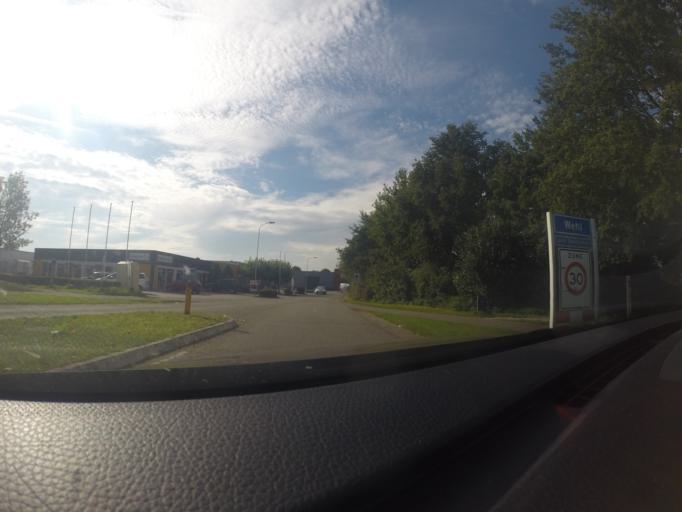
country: NL
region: Gelderland
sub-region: Gemeente Doetinchem
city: Doetinchem
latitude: 51.9593
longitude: 6.2200
